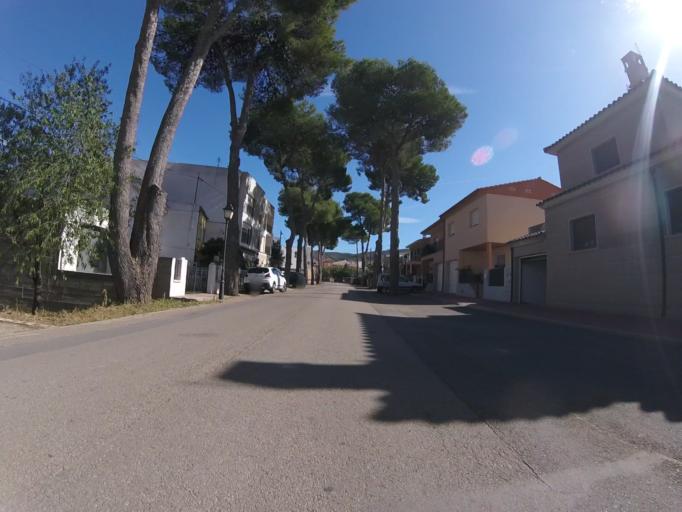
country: ES
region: Valencia
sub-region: Provincia de Castello
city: Santa Magdalena de Pulpis
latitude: 40.3553
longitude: 0.2999
